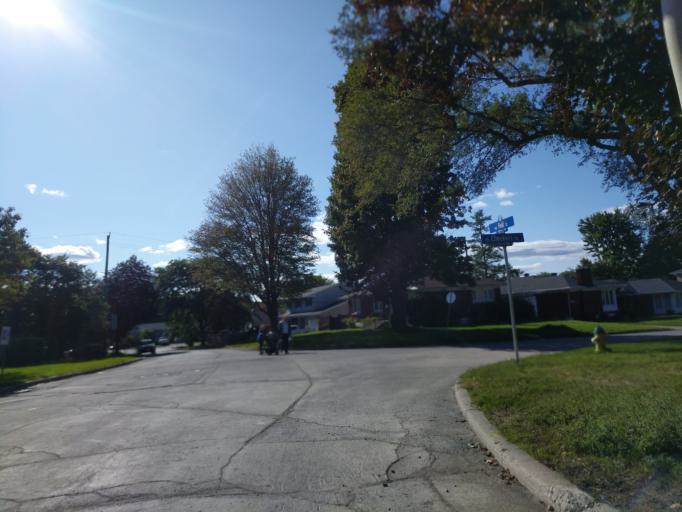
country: CA
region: Ontario
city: Bells Corners
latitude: 45.3548
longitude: -75.7631
